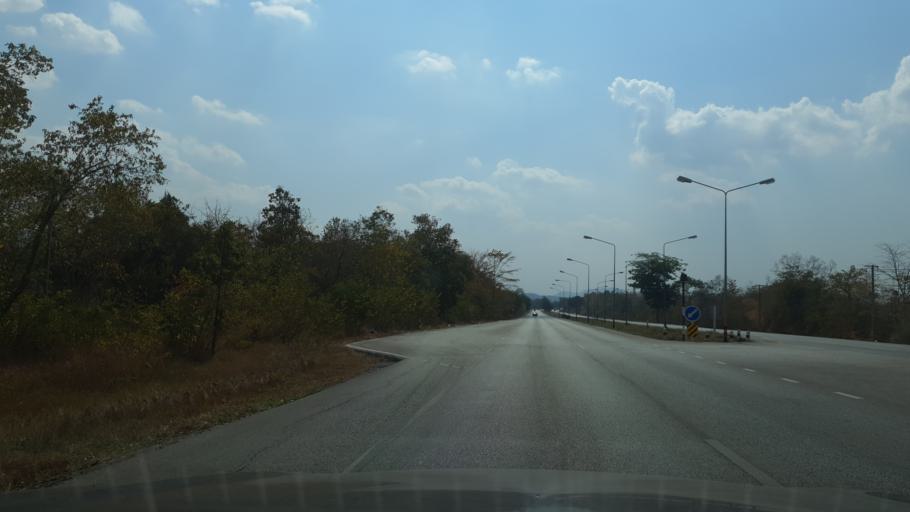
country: TH
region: Lampang
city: Mae Phrik
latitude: 17.4283
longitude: 99.1581
